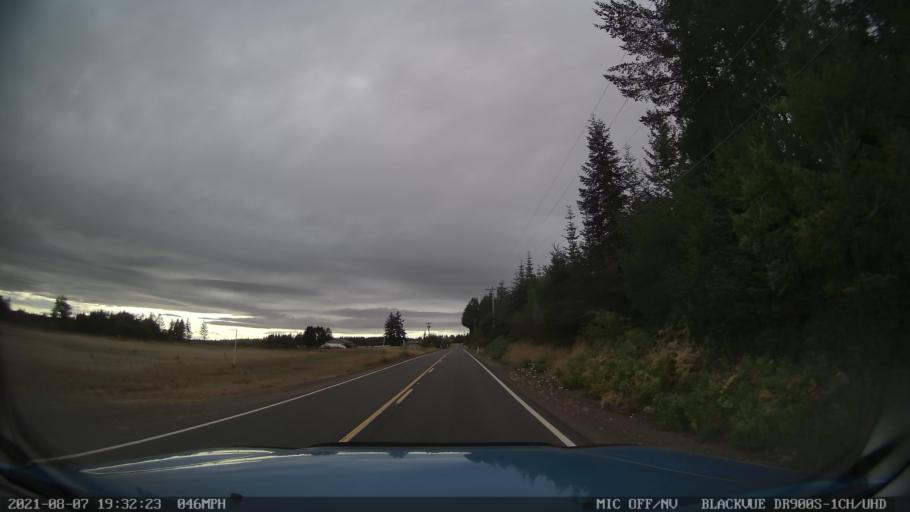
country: US
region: Oregon
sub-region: Linn County
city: Lyons
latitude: 44.8996
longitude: -122.6431
